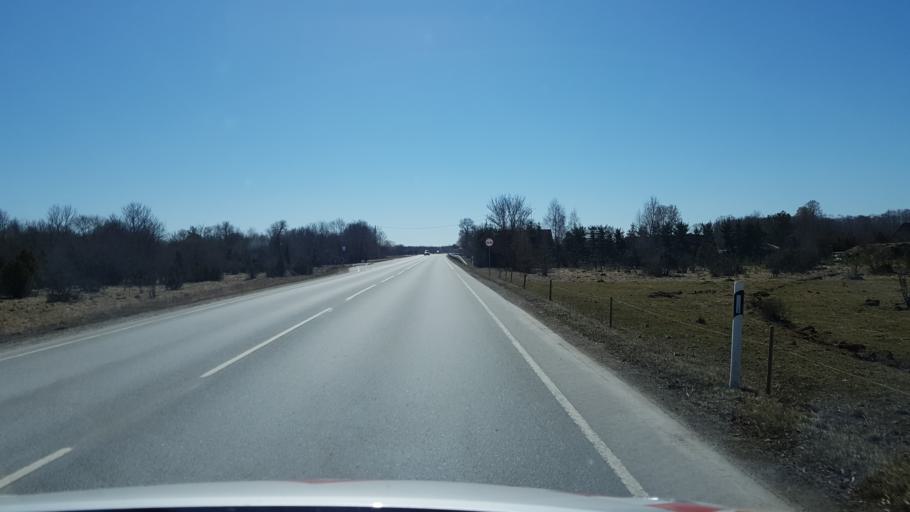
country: EE
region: Laeaene-Virumaa
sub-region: Viru-Nigula vald
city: Kunda
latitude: 59.4738
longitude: 26.4830
